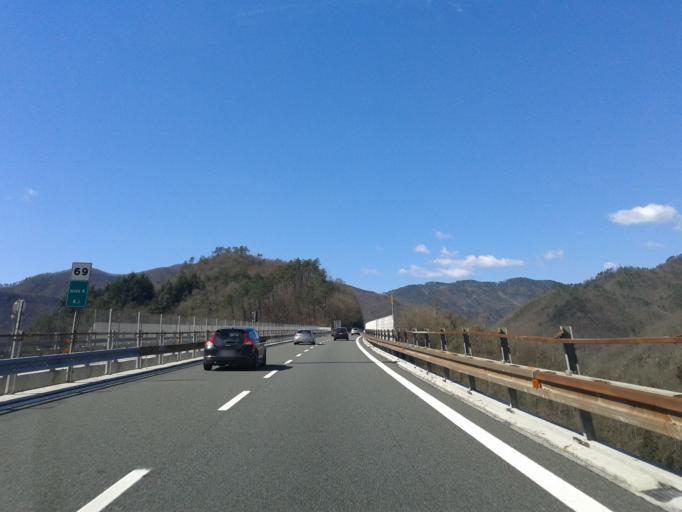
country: IT
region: Liguria
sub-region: Provincia di La Spezia
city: Carrodano
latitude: 44.2339
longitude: 9.6415
